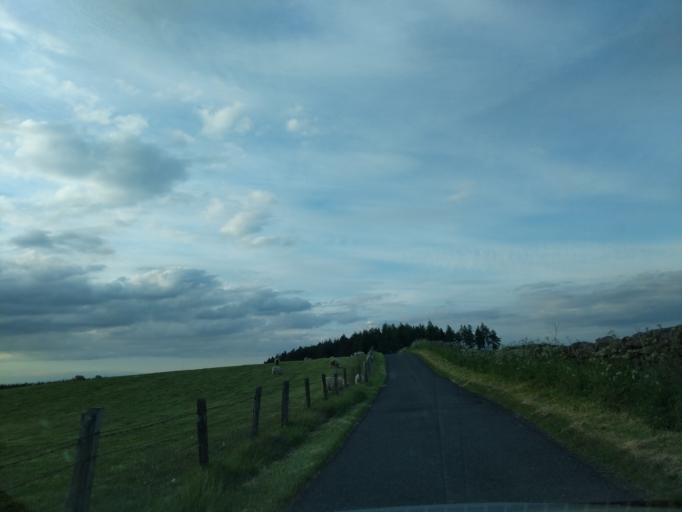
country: GB
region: Scotland
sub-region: Midlothian
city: Gorebridge
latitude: 55.7818
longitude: -3.0983
